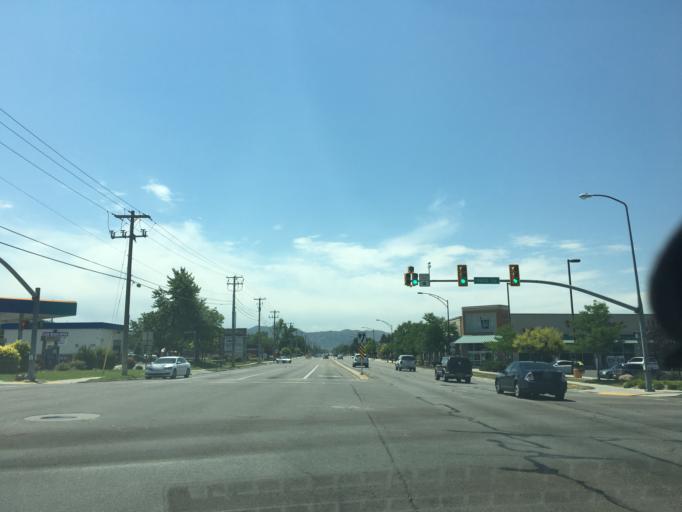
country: US
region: Utah
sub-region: Salt Lake County
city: Sandy City
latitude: 40.5808
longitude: -111.8722
